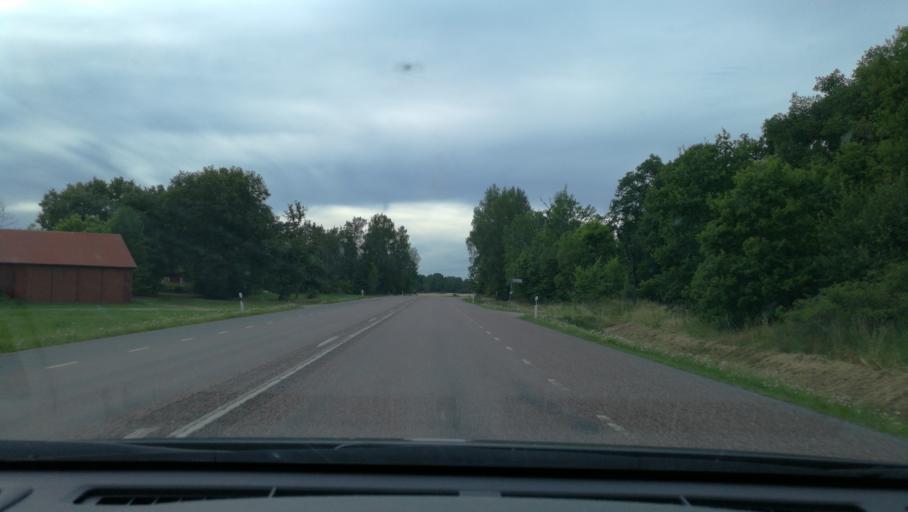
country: SE
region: Vaestmanland
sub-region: Kungsors Kommun
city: Kungsoer
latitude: 59.4414
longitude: 16.0480
